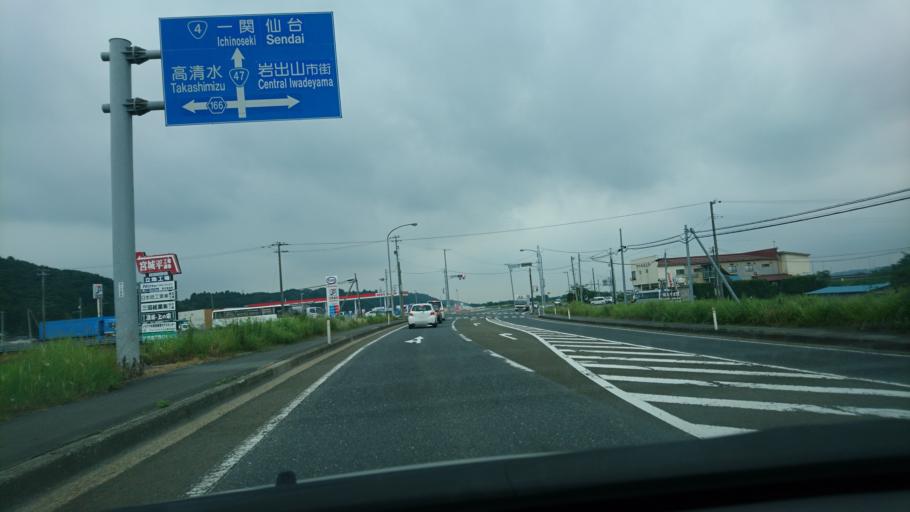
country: JP
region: Miyagi
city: Furukawa
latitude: 38.6582
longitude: 140.8797
